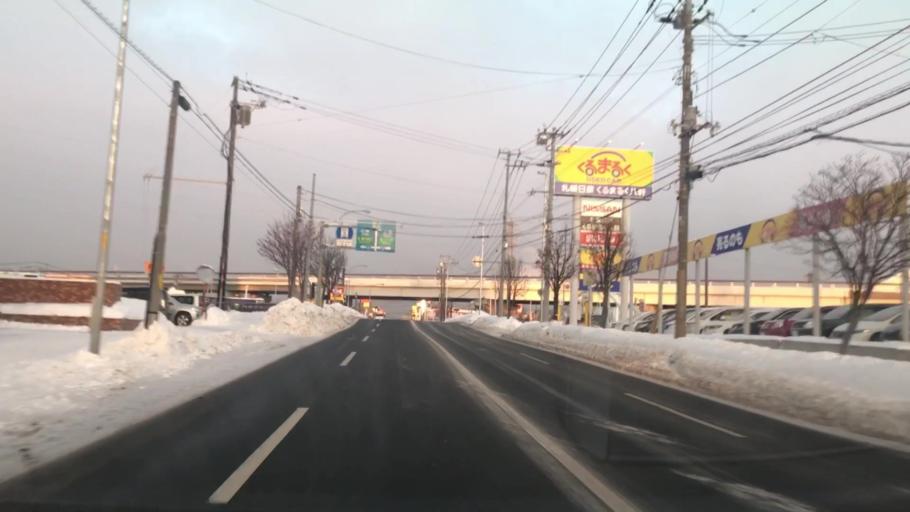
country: JP
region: Hokkaido
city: Sapporo
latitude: 43.0961
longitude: 141.2996
